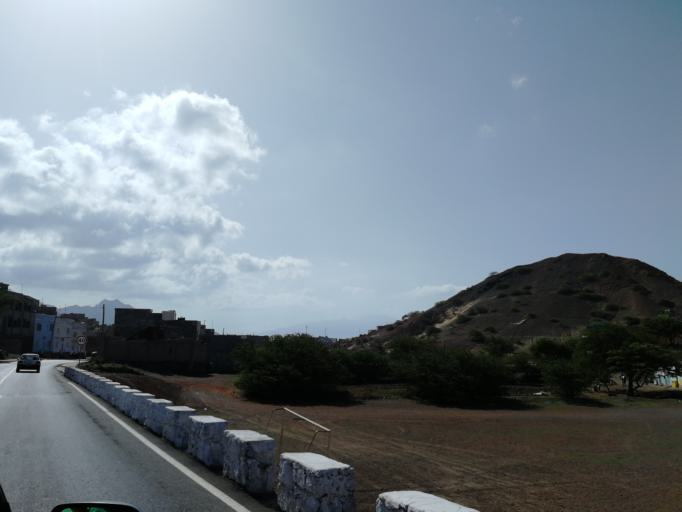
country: CV
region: Sao Vicente
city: Mindelo
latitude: 16.8805
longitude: -24.9691
